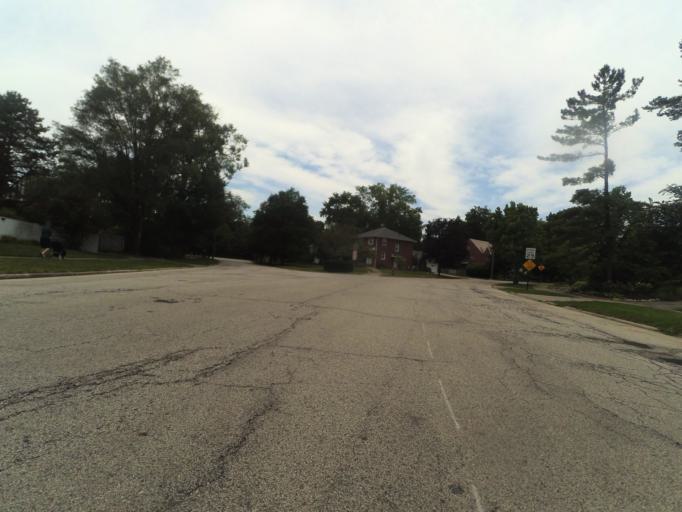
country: US
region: Ohio
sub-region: Cuyahoga County
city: University Heights
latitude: 41.4867
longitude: -81.5416
